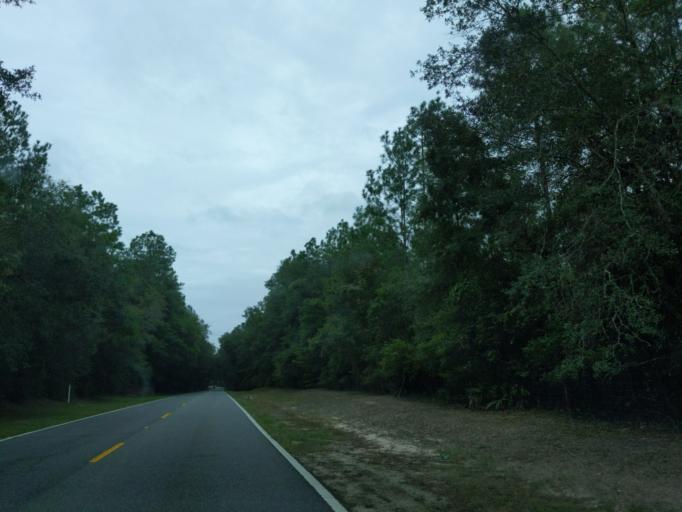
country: US
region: Florida
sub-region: Leon County
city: Woodville
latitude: 30.3673
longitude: -84.1553
